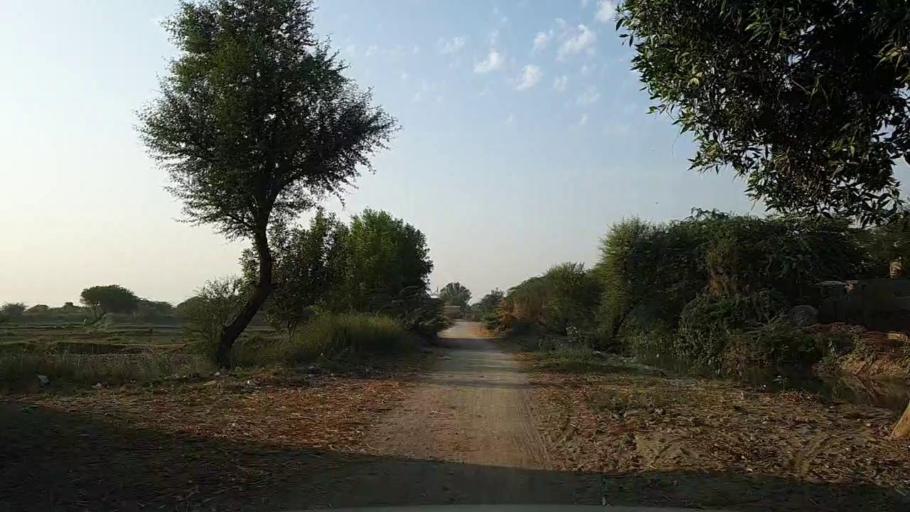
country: PK
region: Sindh
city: Daro Mehar
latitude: 24.7758
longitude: 68.1965
